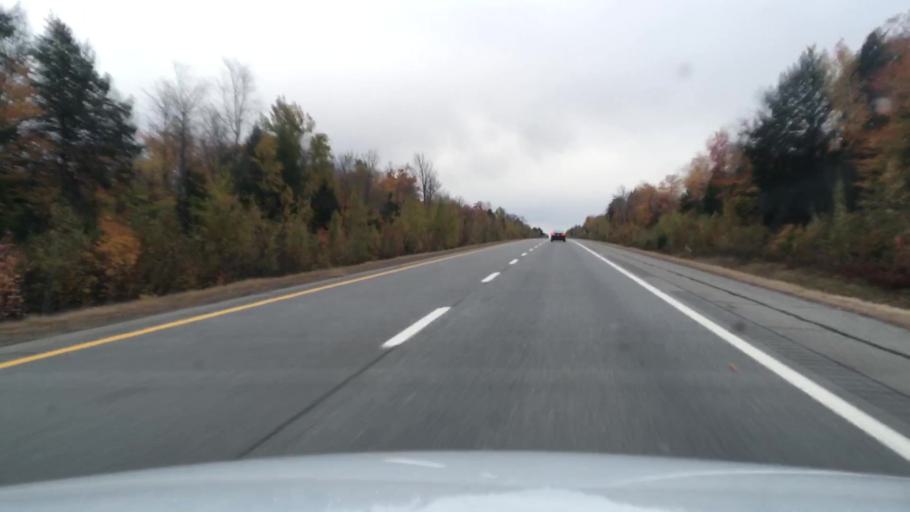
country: US
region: Maine
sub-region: Penobscot County
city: Greenbush
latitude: 45.0918
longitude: -68.6952
